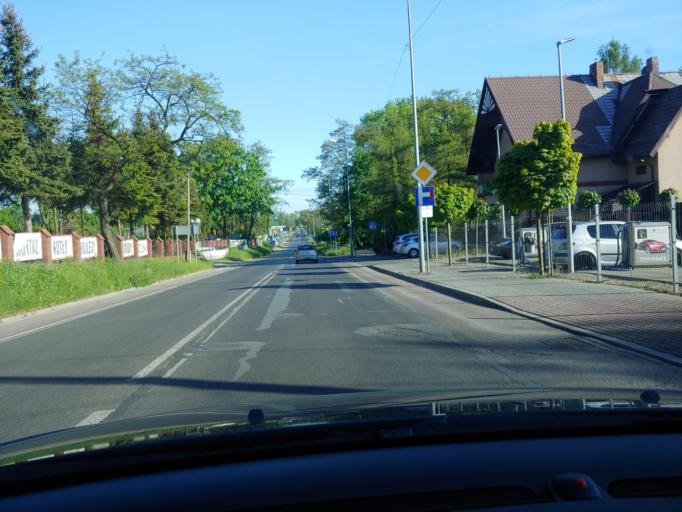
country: PL
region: Silesian Voivodeship
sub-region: Jaworzno
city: Jaworzno
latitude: 50.1962
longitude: 19.2818
